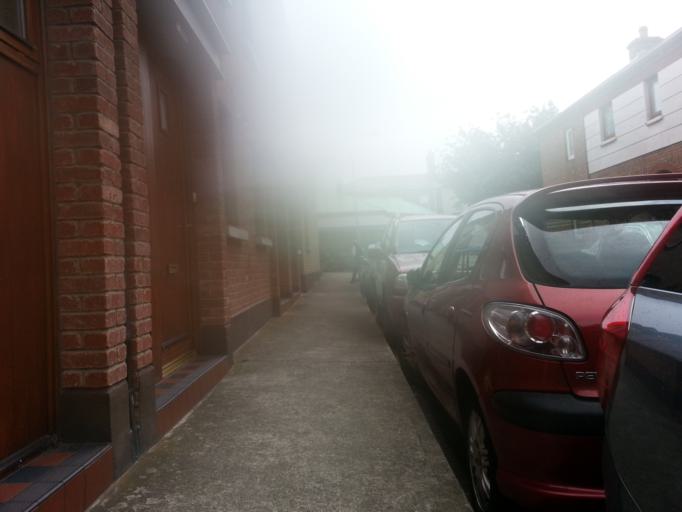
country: IE
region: Leinster
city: Rathmines
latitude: 53.3364
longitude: -6.2708
